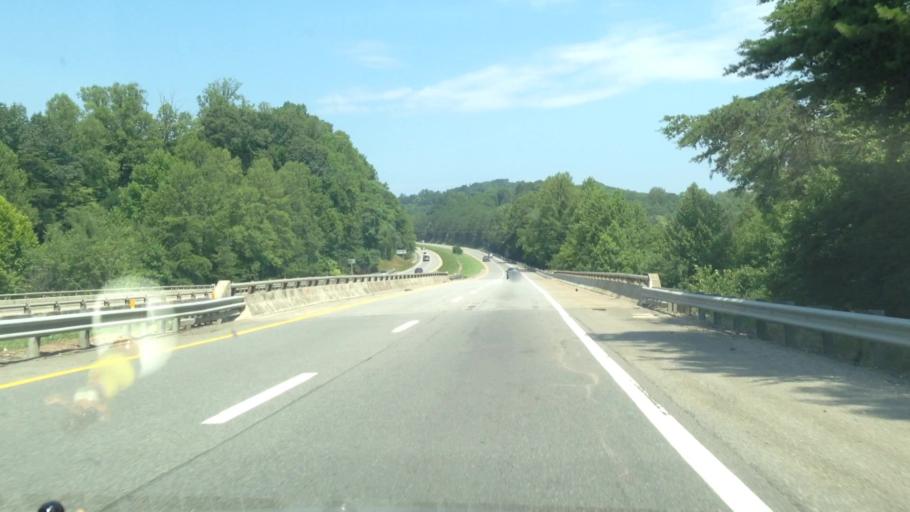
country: US
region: Virginia
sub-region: Henry County
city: Collinsville
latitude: 36.6841
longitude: -79.9390
